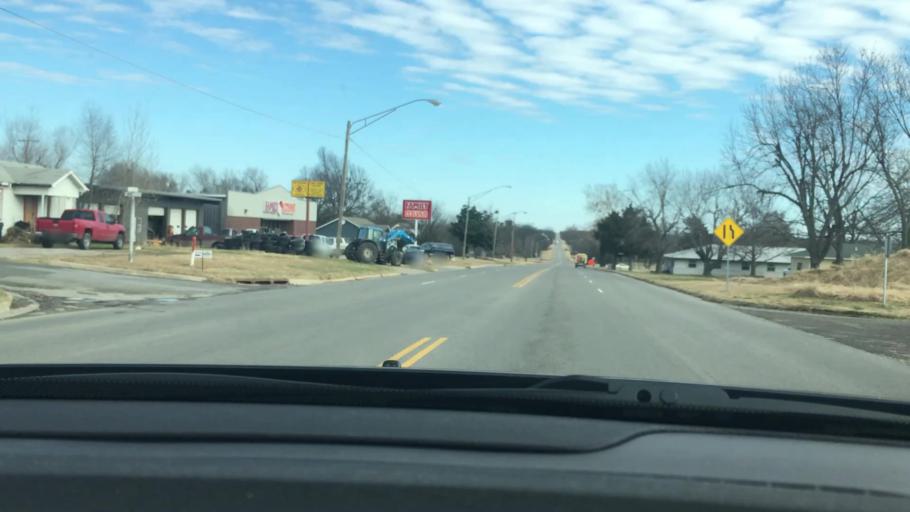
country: US
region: Oklahoma
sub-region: Garvin County
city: Stratford
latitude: 34.7968
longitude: -96.9525
